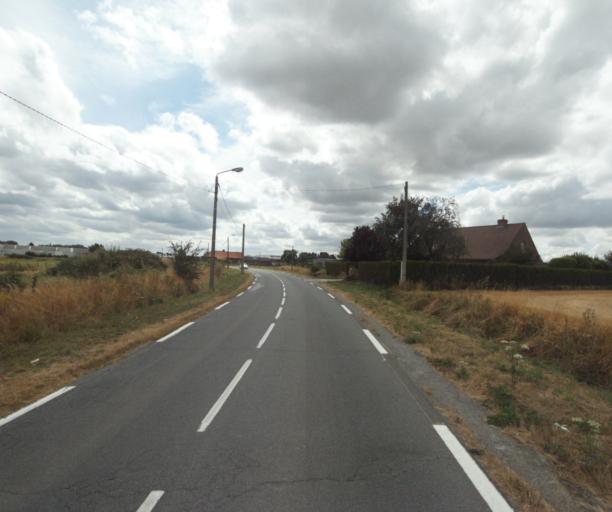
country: FR
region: Nord-Pas-de-Calais
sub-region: Departement du Nord
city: Linselles
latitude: 50.7533
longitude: 3.0846
